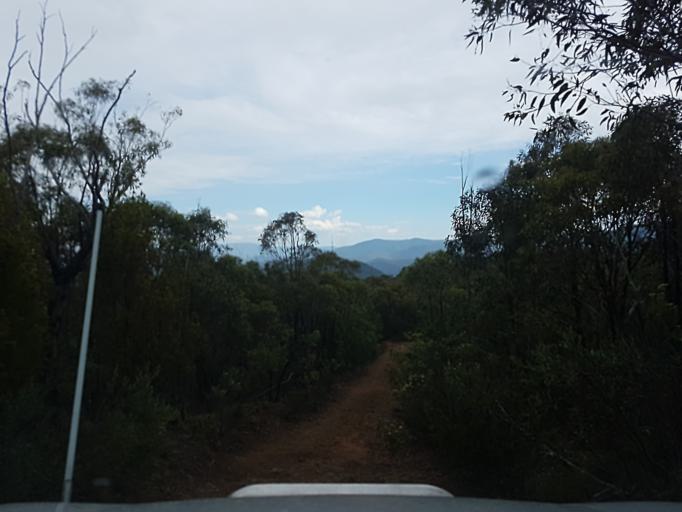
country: AU
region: New South Wales
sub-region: Snowy River
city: Jindabyne
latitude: -36.9221
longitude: 148.3420
